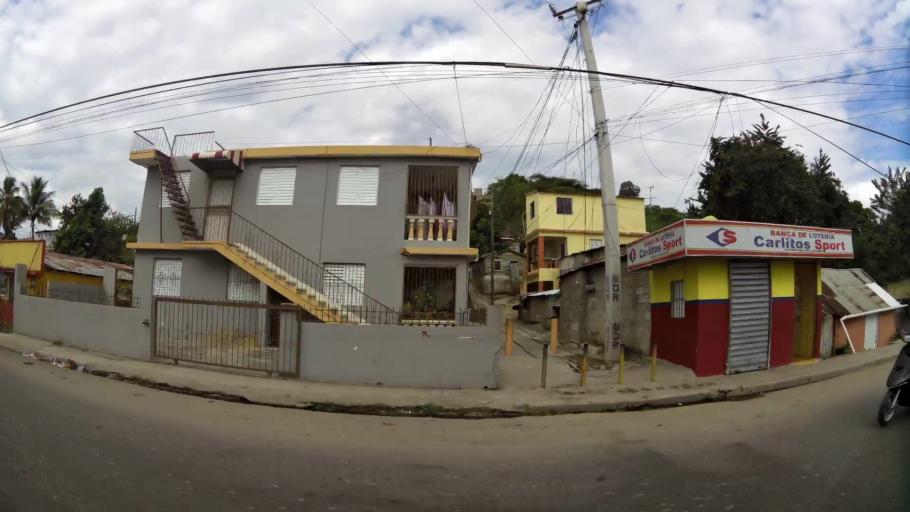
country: DO
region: Santiago
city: Santiago de los Caballeros
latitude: 19.4344
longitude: -70.7057
